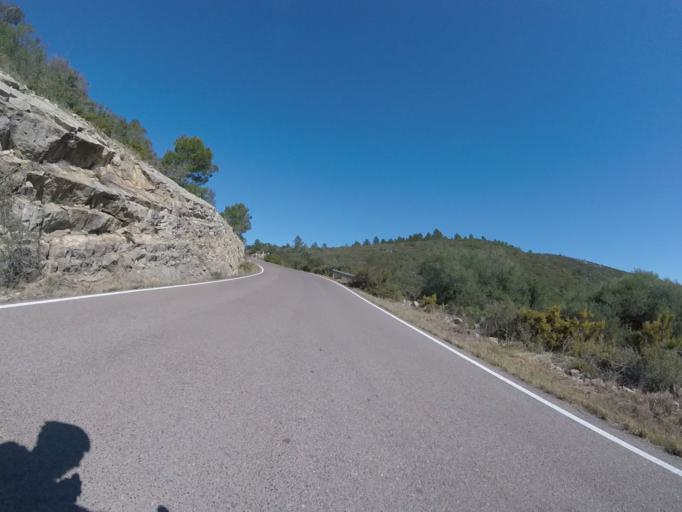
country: ES
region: Valencia
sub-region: Provincia de Castello
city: Santa Magdalena de Pulpis
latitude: 40.3852
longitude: 0.2539
